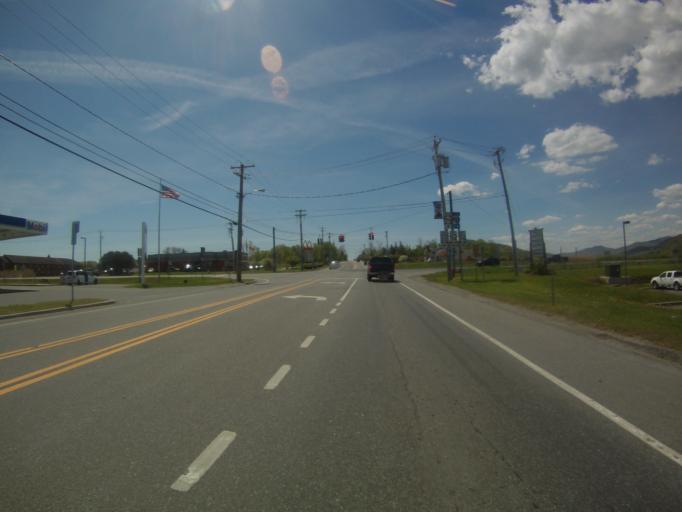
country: US
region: New York
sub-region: Essex County
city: Ticonderoga
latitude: 43.8592
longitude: -73.4380
